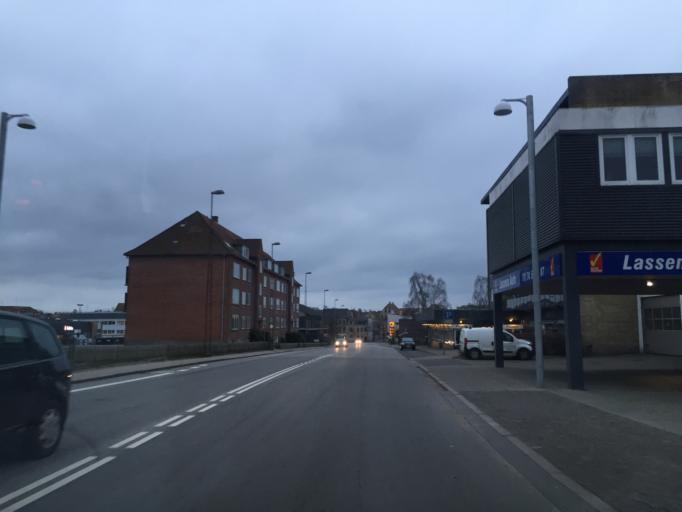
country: DK
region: South Denmark
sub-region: Haderslev Kommune
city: Haderslev
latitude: 55.2534
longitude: 9.4904
